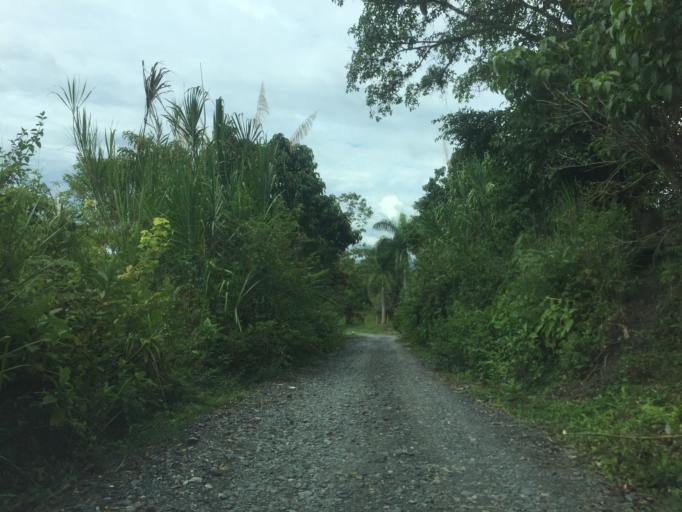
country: CO
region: Santander
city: Guepsa
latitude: 6.0211
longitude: -73.5505
